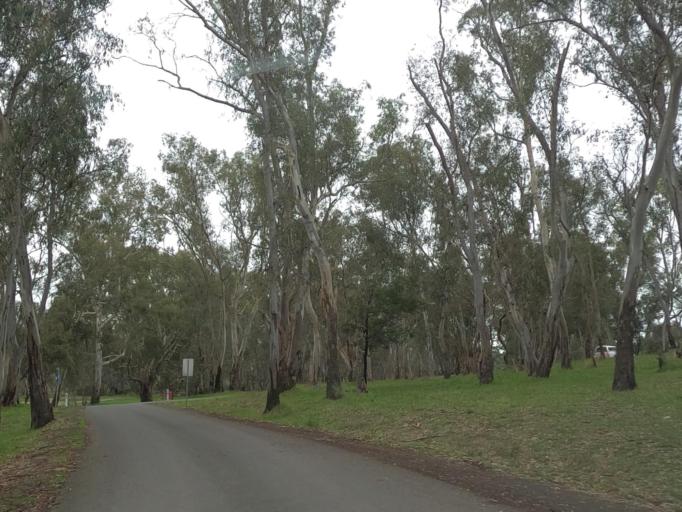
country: AU
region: Victoria
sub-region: Greater Bendigo
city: Kangaroo Flat
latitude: -36.8406
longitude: 144.1556
